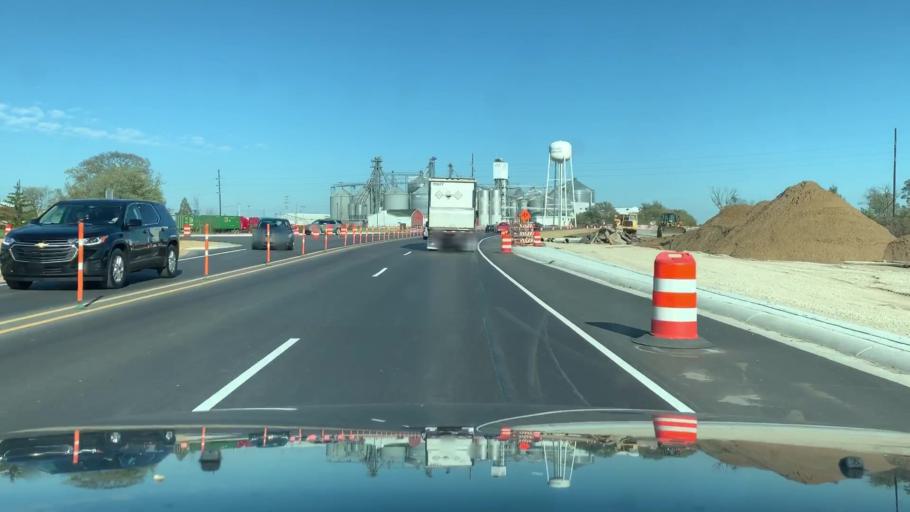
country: US
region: Michigan
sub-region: Ottawa County
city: Zeeland
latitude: 42.8114
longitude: -85.9929
